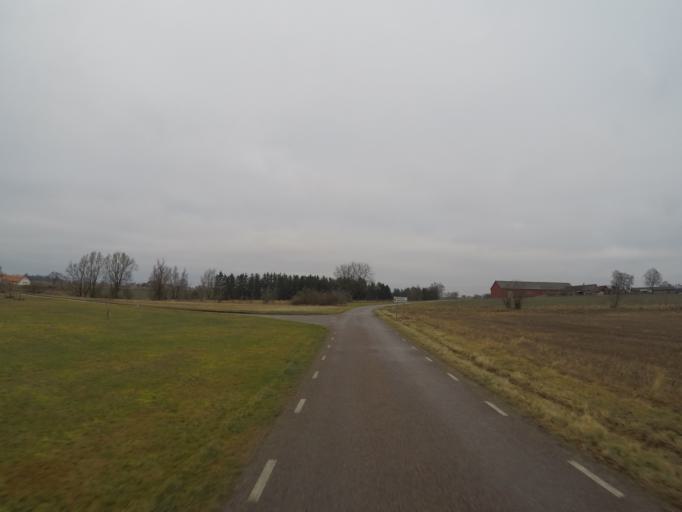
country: SE
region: Skane
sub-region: Hoors Kommun
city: Loberod
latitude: 55.7584
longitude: 13.3975
